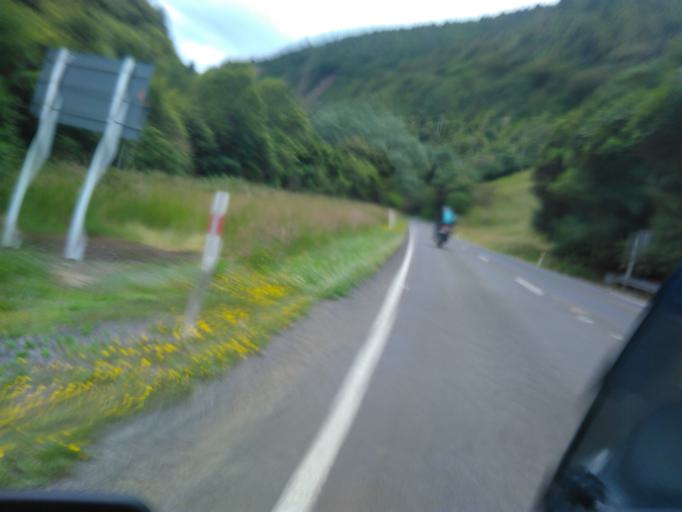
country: NZ
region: Bay of Plenty
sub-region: Opotiki District
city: Opotiki
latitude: -38.3416
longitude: 177.4280
